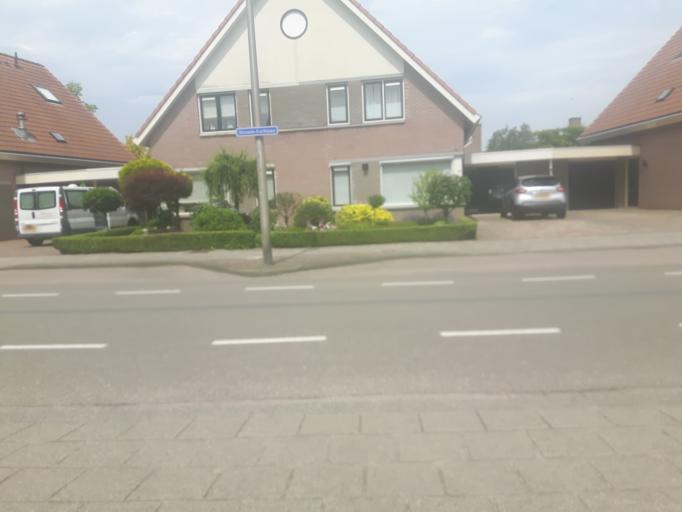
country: NL
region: Overijssel
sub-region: Gemeente Borne
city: Borne
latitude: 52.3099
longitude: 6.7487
